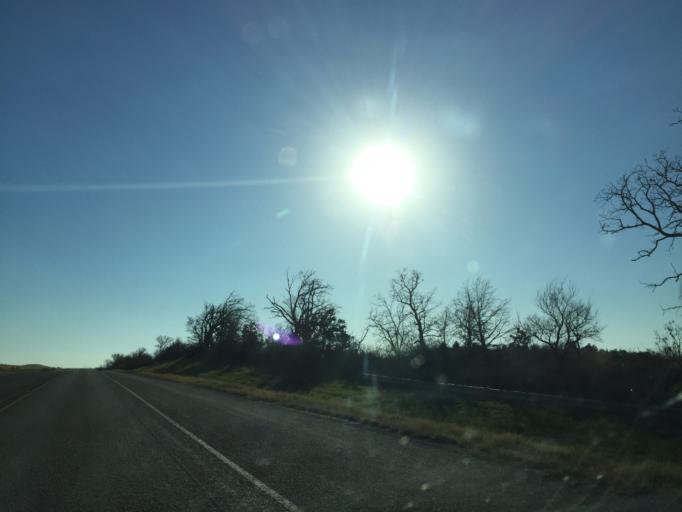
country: US
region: Texas
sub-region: Bastrop County
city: Elgin
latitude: 30.3640
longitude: -97.2658
